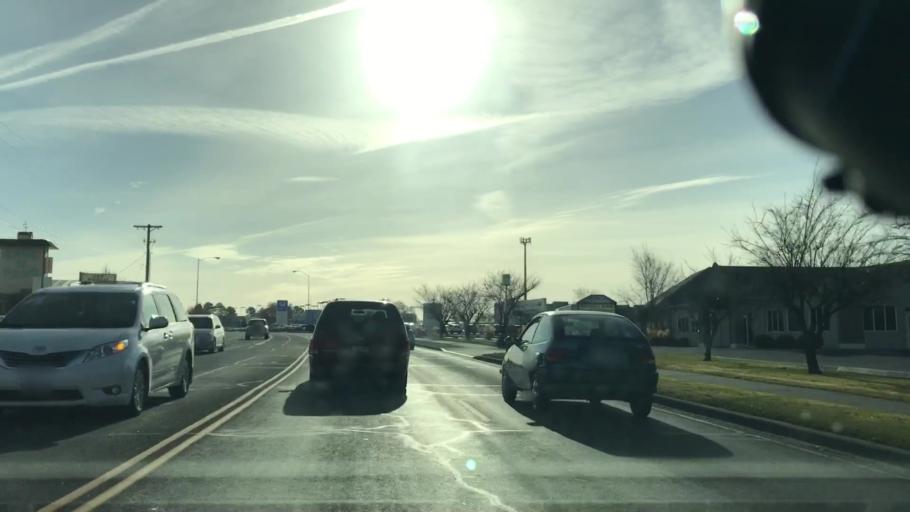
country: US
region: Washington
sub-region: Grant County
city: Moses Lake
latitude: 47.1208
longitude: -119.2676
